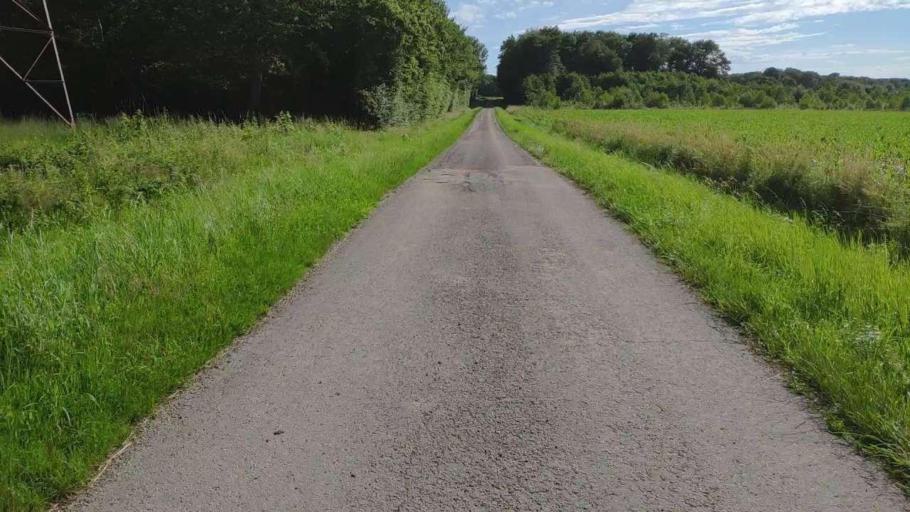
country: FR
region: Franche-Comte
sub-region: Departement du Jura
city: Bletterans
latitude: 46.8241
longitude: 5.5273
